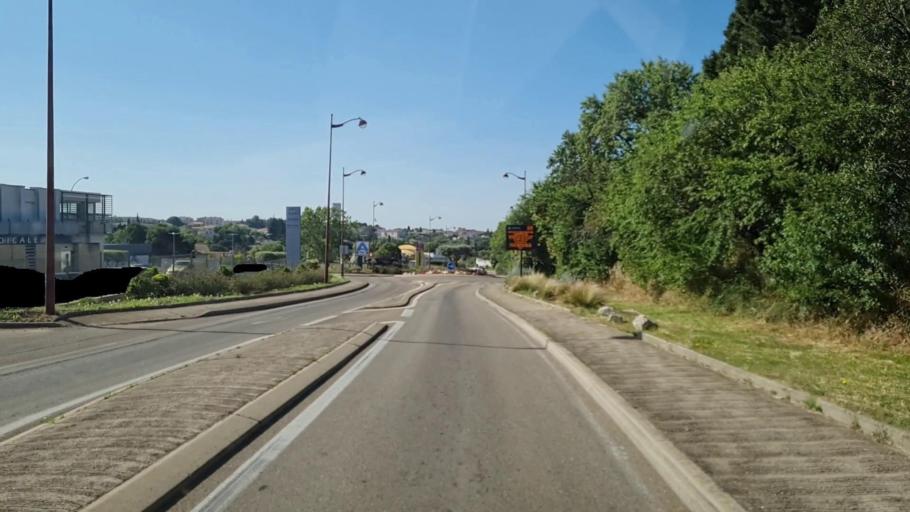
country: FR
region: Languedoc-Roussillon
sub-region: Departement du Gard
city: Saint-Gilles
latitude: 43.6878
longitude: 4.4278
